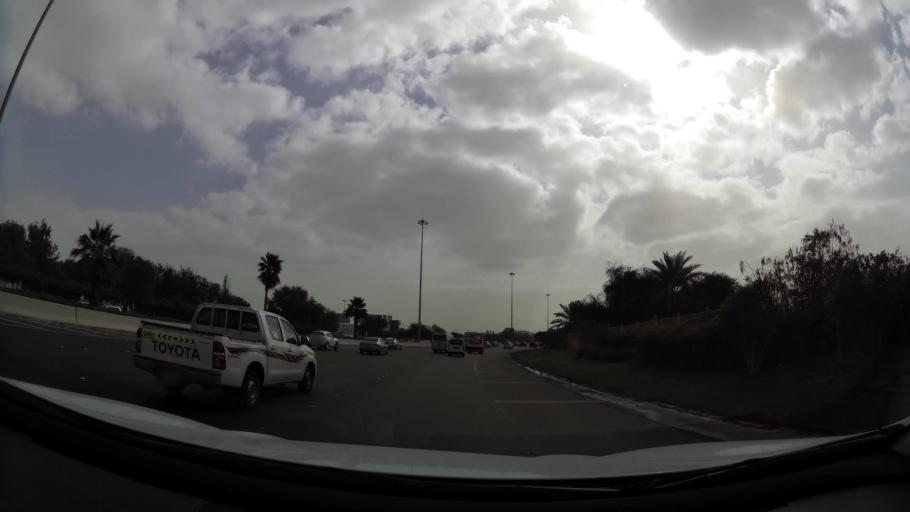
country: AE
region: Abu Dhabi
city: Abu Dhabi
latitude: 24.4205
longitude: 54.4897
